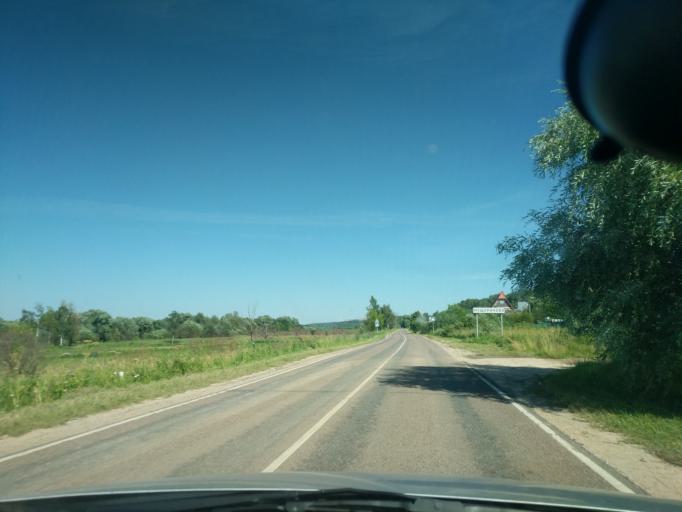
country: RU
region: Moskovskaya
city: Pushchino
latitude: 54.8436
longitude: 37.5364
